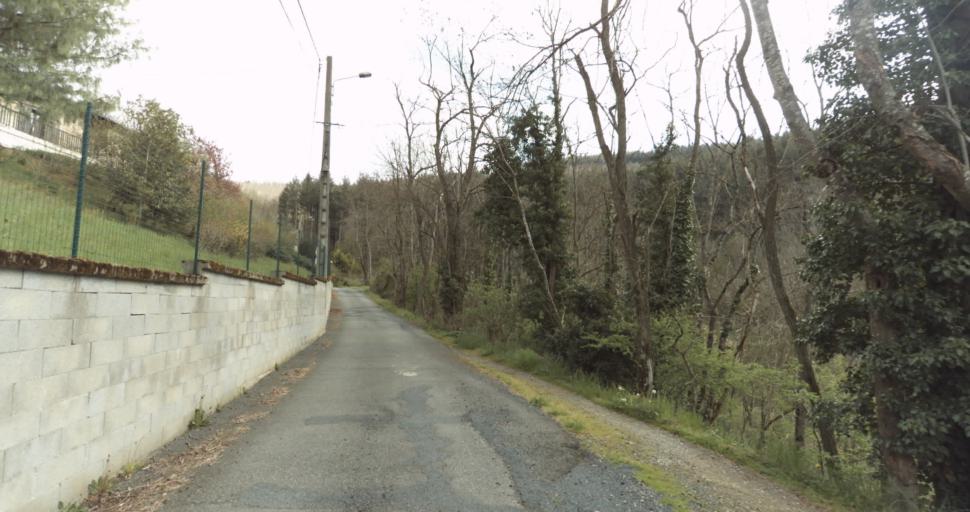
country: FR
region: Rhone-Alpes
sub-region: Departement du Rhone
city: Tarare
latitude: 45.9033
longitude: 4.4439
